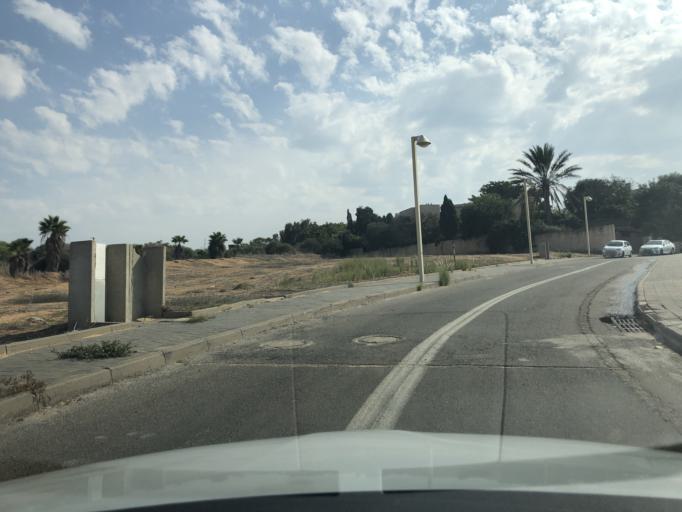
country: IL
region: Tel Aviv
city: Kefar Shemaryahu
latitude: 32.2162
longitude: 34.8177
